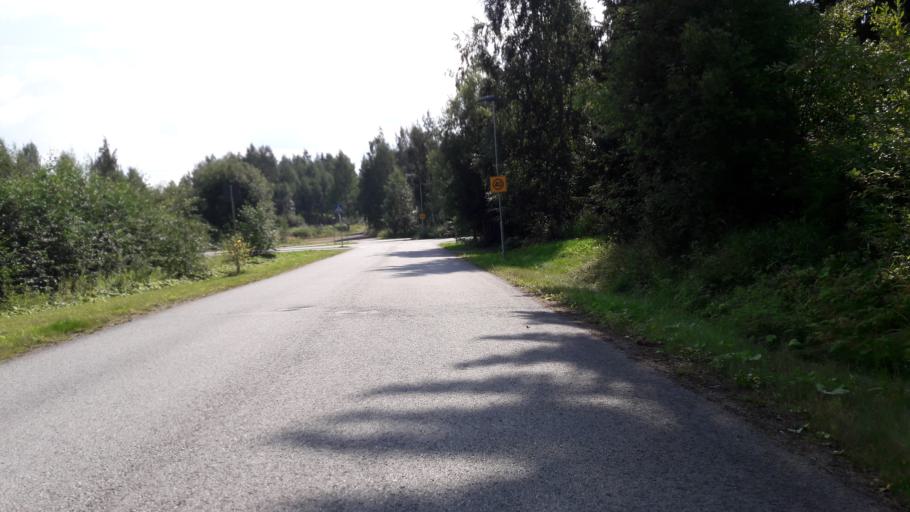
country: FI
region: North Karelia
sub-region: Joensuu
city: Joensuu
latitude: 62.5305
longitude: 29.8501
